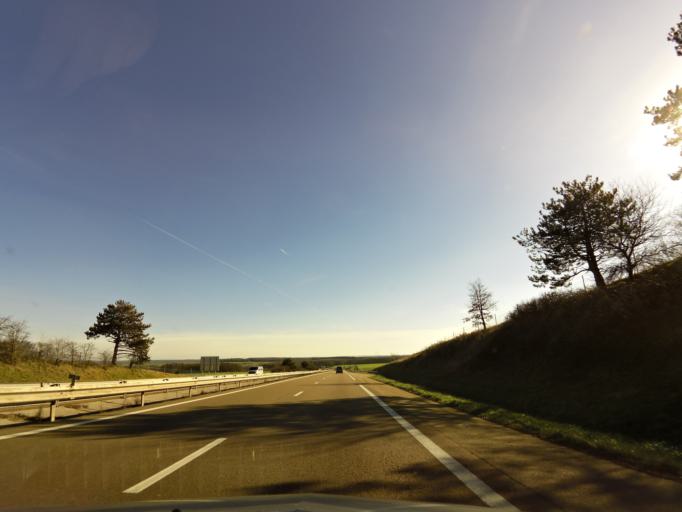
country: FR
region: Bourgogne
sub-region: Departement de l'Yonne
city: Vermenton
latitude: 47.7257
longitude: 3.7500
